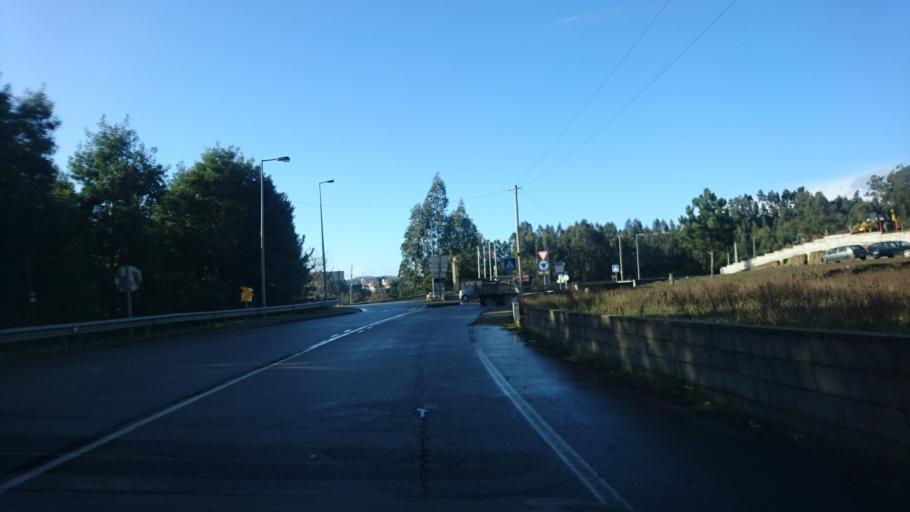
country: PT
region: Porto
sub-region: Paredes
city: Recarei
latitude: 41.1487
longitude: -8.3937
